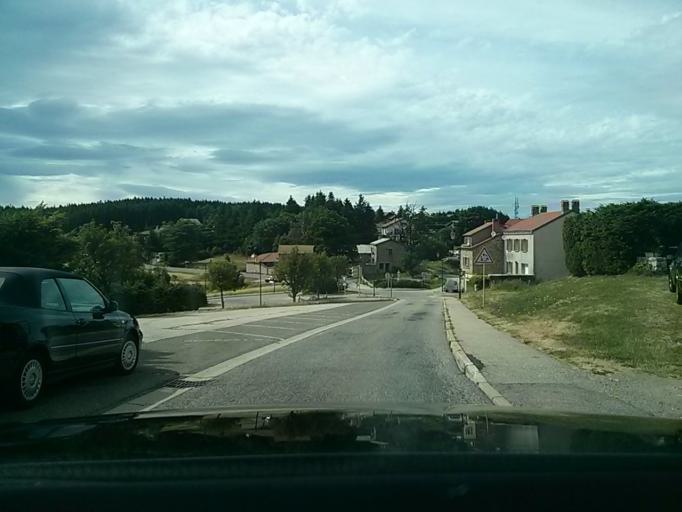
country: FR
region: Rhone-Alpes
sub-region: Departement de la Loire
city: Bourg-Argental
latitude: 45.3698
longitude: 4.5136
